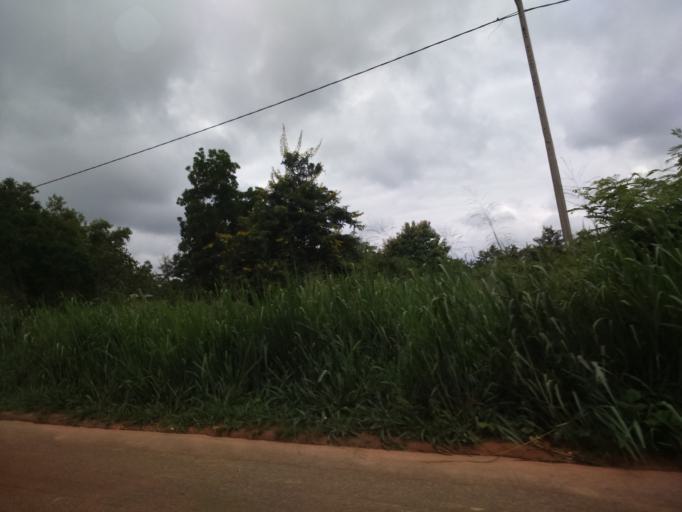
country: CI
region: Moyen-Comoe
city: Abengourou
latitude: 6.6289
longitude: -3.7106
